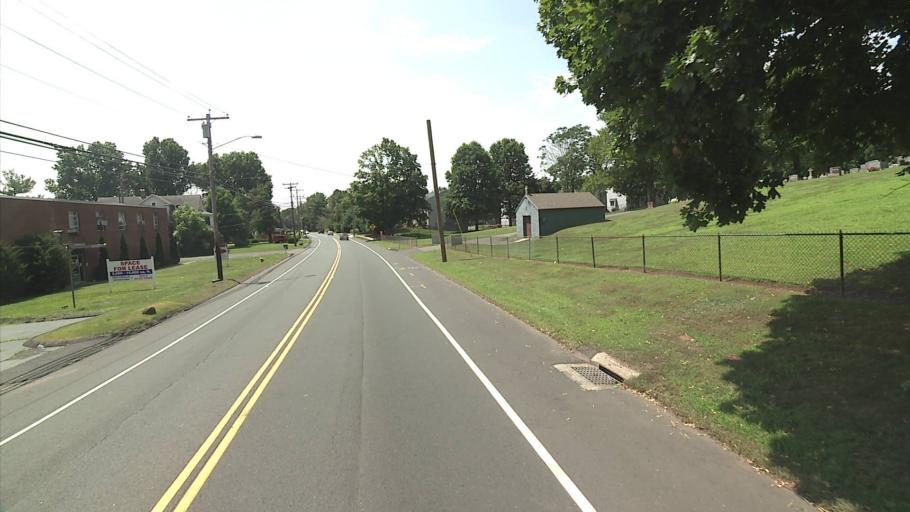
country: US
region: Connecticut
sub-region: New Haven County
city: Meriden
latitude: 41.5143
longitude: -72.8158
